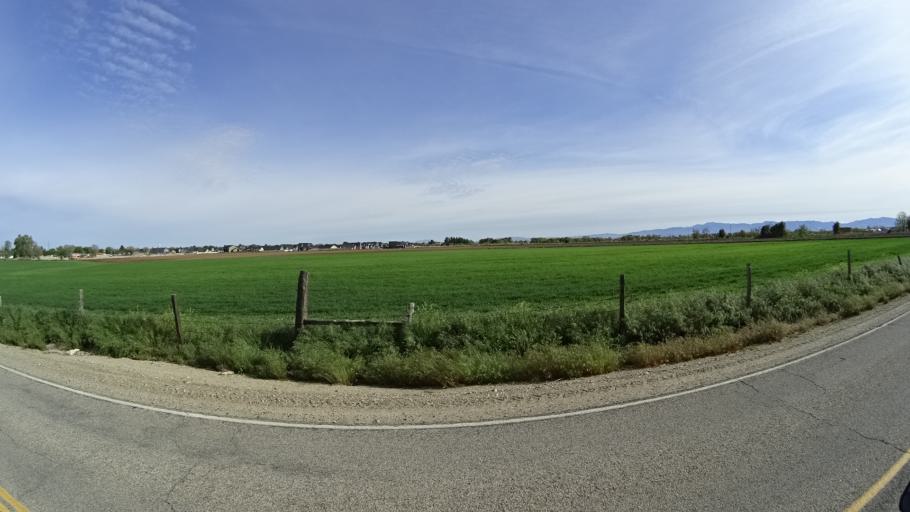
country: US
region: Idaho
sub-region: Ada County
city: Kuna
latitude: 43.4734
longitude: -116.3982
